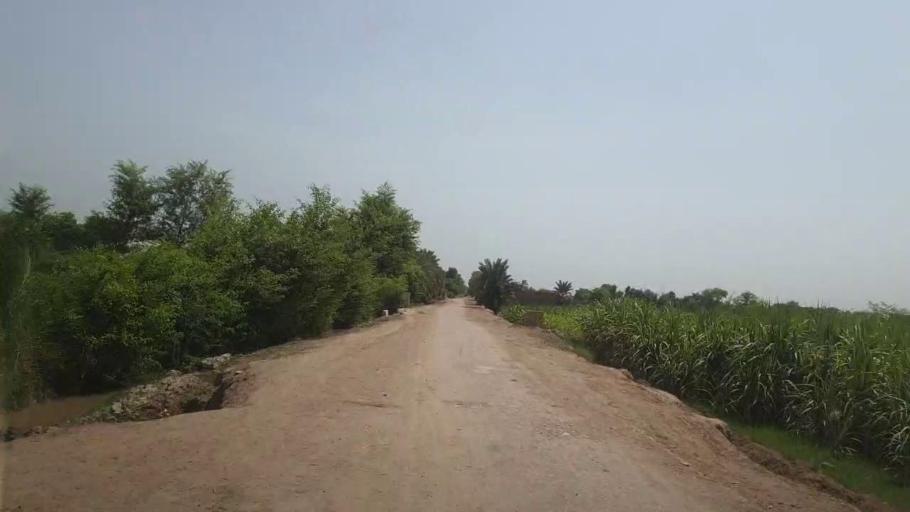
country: PK
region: Sindh
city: Sobhadero
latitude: 27.4408
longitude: 68.4027
